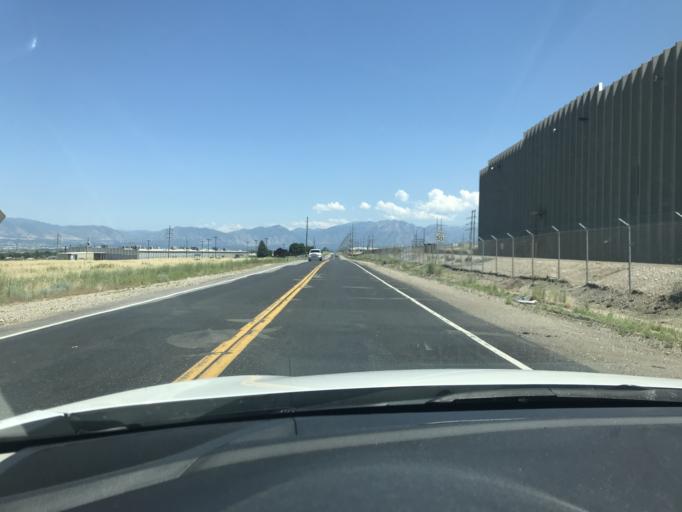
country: US
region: Utah
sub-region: Salt Lake County
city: Magna
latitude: 40.6820
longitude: -112.0810
